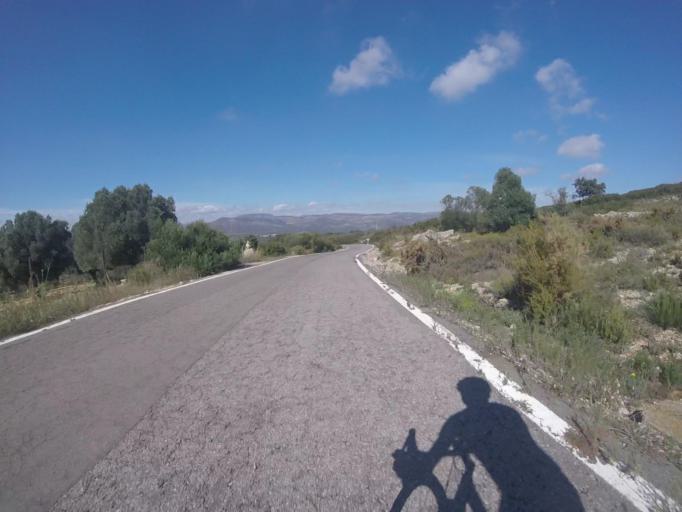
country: ES
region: Valencia
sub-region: Provincia de Castello
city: Albocasser
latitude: 40.3542
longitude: 0.0420
